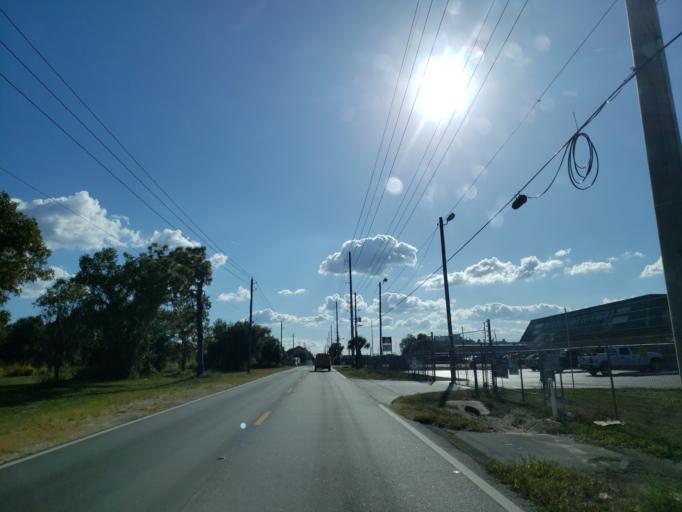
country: US
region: Florida
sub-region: Hillsborough County
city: Plant City
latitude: 27.9975
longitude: -82.1535
